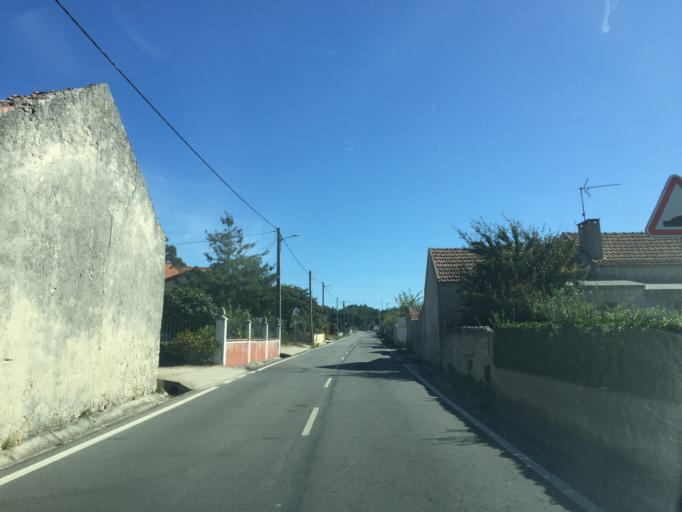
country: PT
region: Coimbra
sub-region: Figueira da Foz
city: Alhadas
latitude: 40.2208
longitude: -8.8190
